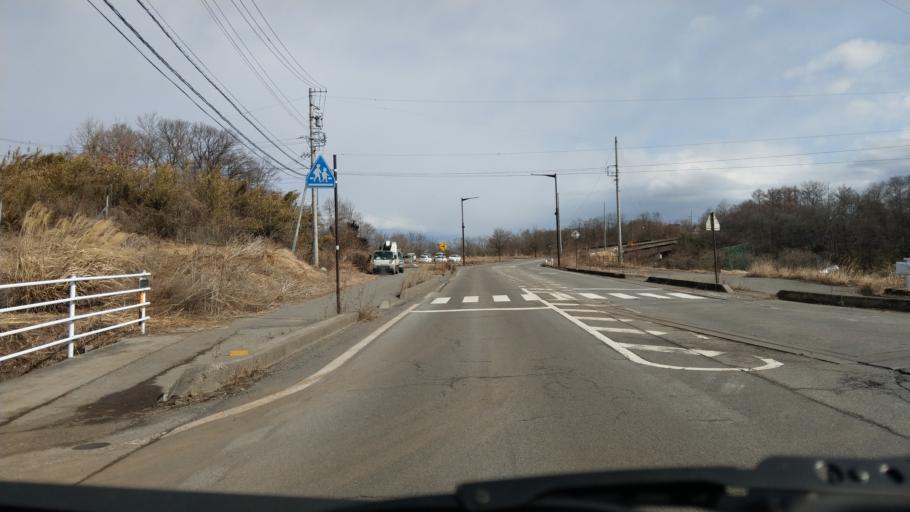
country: JP
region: Nagano
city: Komoro
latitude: 36.2826
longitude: 138.4032
